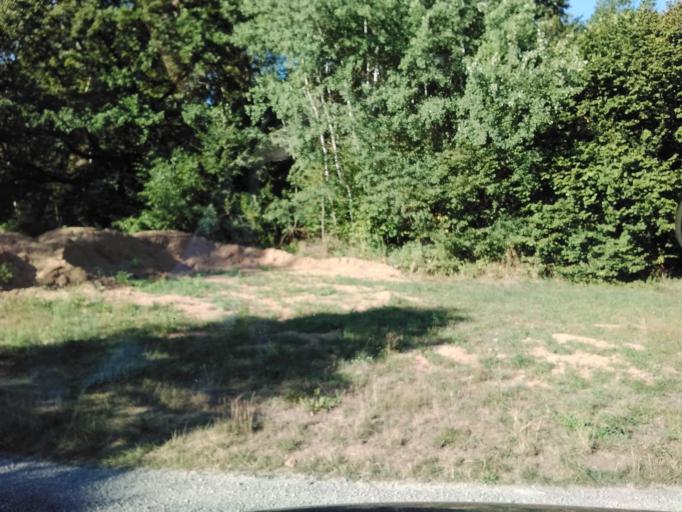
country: DE
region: Bavaria
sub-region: Regierungsbezirk Unterfranken
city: Stadtprozelten
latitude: 49.7865
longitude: 9.4277
